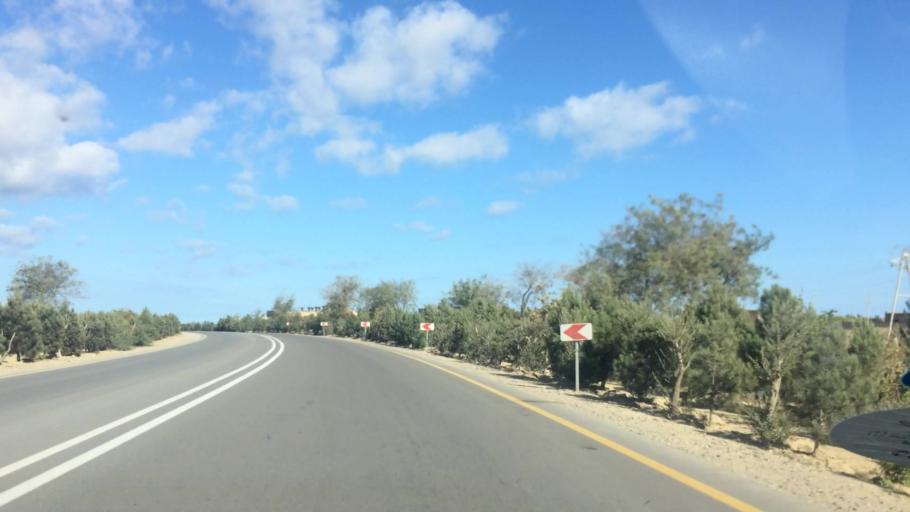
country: AZ
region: Baki
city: Pirallahi
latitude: 40.4232
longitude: 50.3566
